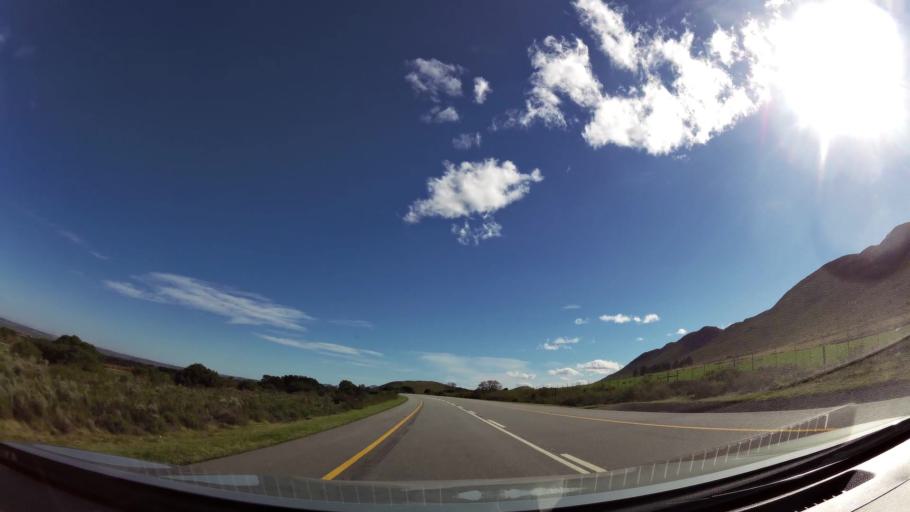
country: ZA
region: Eastern Cape
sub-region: Cacadu District Municipality
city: Kruisfontein
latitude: -33.9938
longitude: 24.6984
